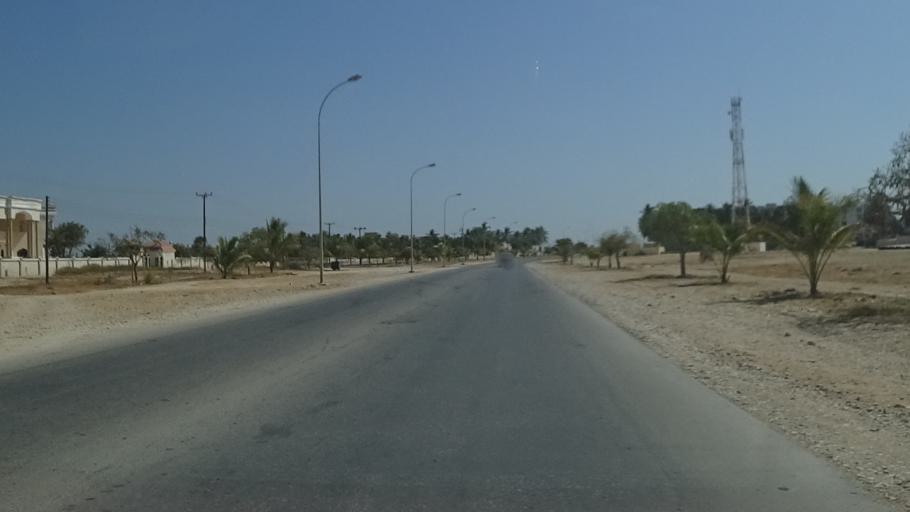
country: OM
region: Zufar
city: Salalah
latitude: 17.0423
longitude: 54.1707
